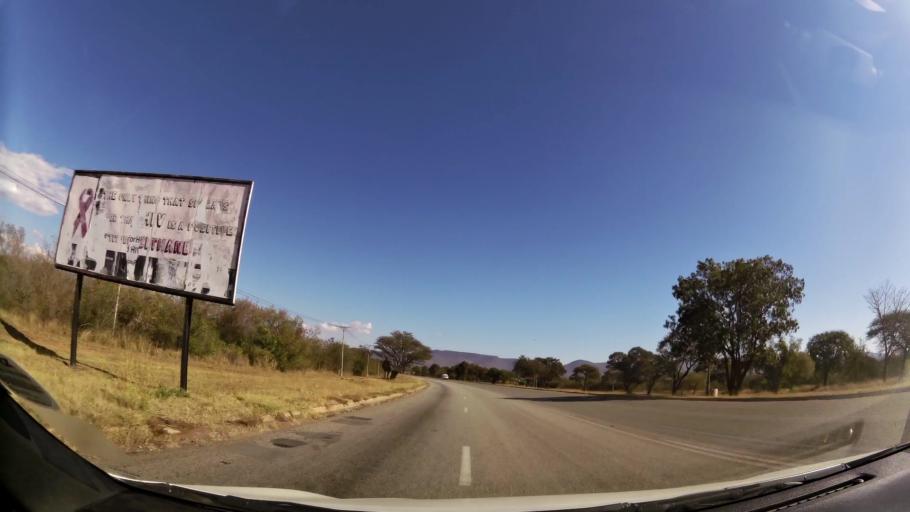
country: ZA
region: Limpopo
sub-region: Waterberg District Municipality
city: Mokopane
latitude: -24.1666
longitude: 29.0202
